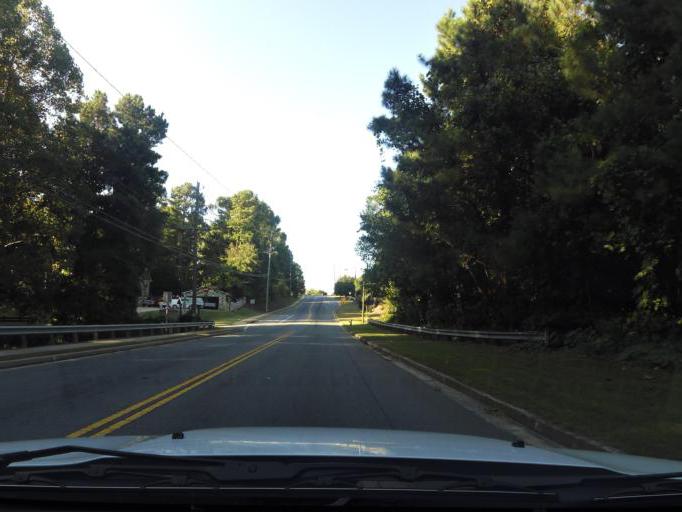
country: US
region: Georgia
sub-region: Cobb County
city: Kennesaw
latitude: 34.0446
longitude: -84.6161
